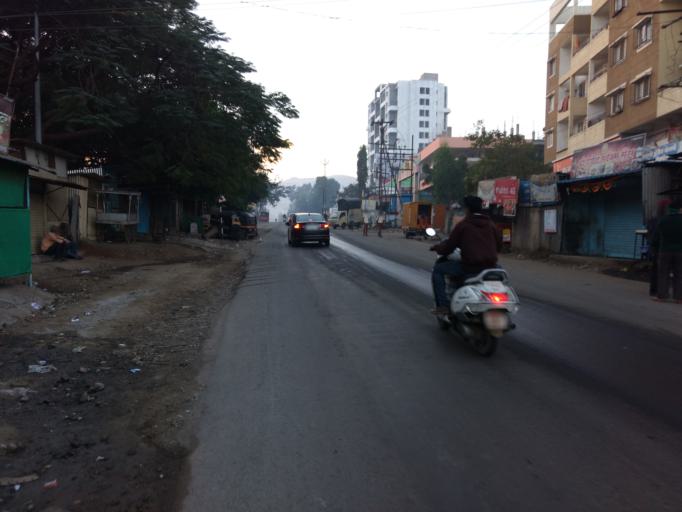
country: IN
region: Maharashtra
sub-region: Pune Division
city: Pune
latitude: 18.4368
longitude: 73.8962
